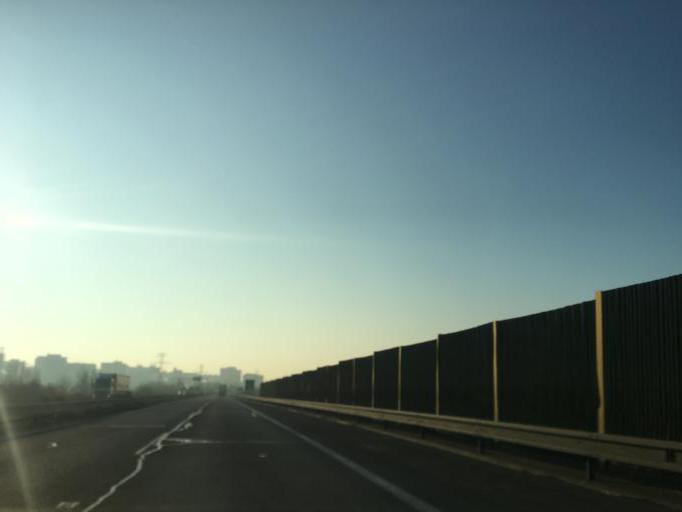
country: AT
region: Burgenland
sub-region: Politischer Bezirk Neusiedl am See
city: Kittsee
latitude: 48.1064
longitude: 17.0893
